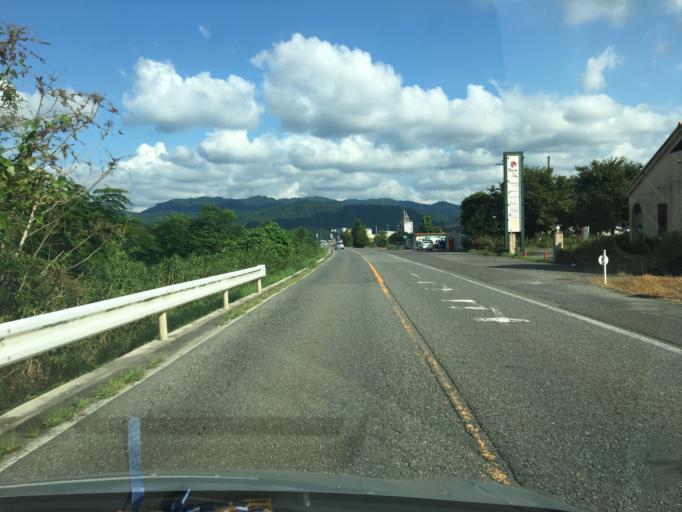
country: JP
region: Hyogo
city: Toyooka
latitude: 35.4432
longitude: 134.7771
